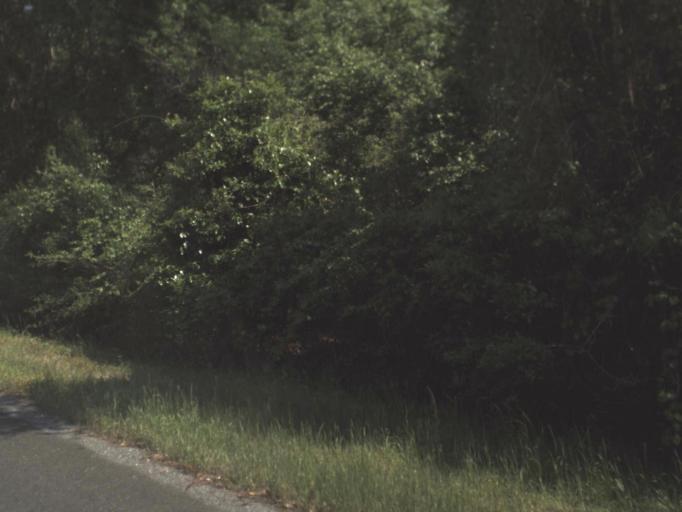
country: US
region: Florida
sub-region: Escambia County
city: Myrtle Grove
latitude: 30.3978
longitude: -87.4092
